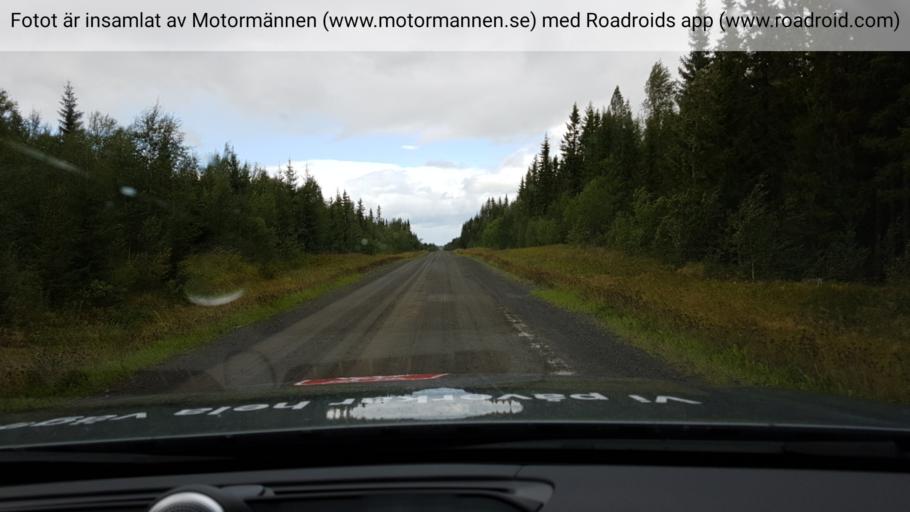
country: SE
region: Jaemtland
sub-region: OEstersunds Kommun
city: Lit
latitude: 63.6621
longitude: 14.9095
